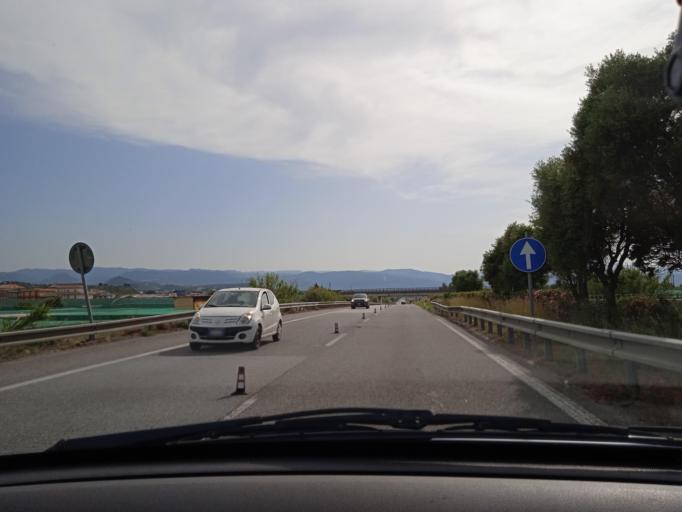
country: IT
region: Sicily
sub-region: Messina
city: Terme
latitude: 38.1429
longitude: 15.1638
